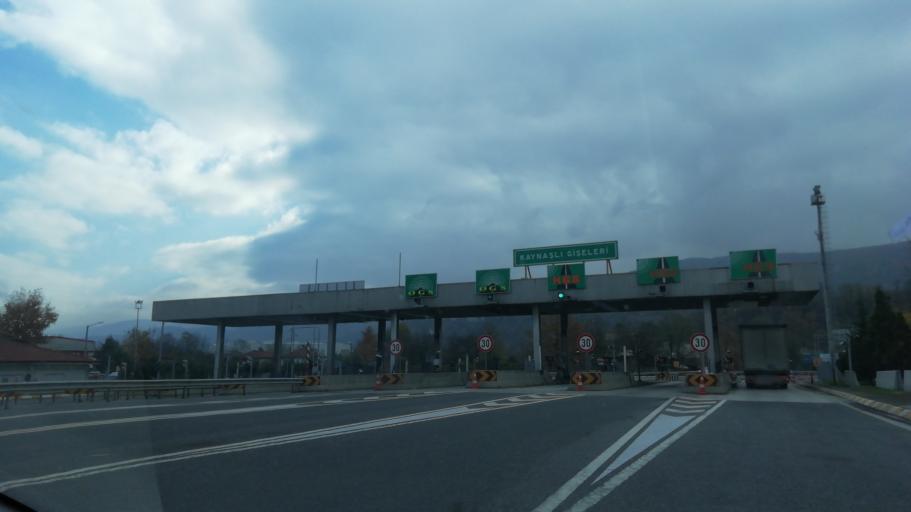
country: TR
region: Duzce
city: Kaynasli
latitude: 40.7843
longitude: 31.2774
